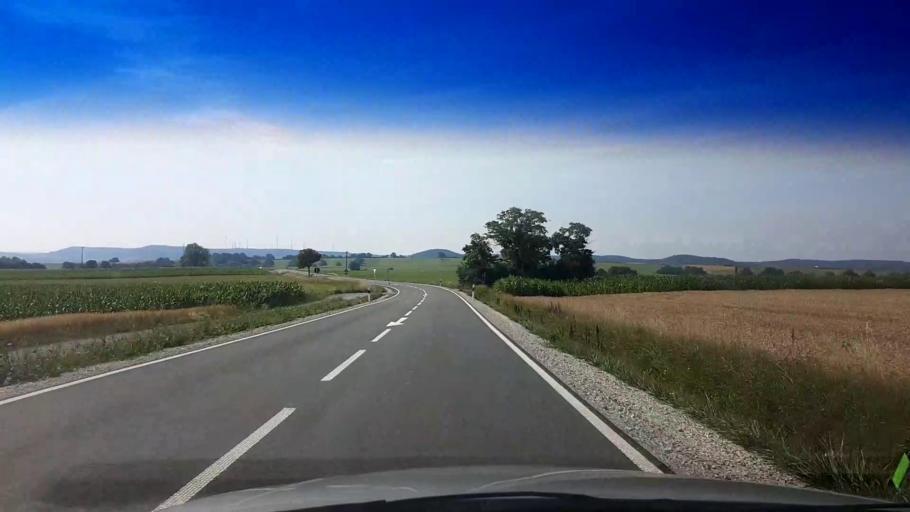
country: DE
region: Bavaria
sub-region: Upper Franconia
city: Mistelgau
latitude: 49.9345
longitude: 11.4722
